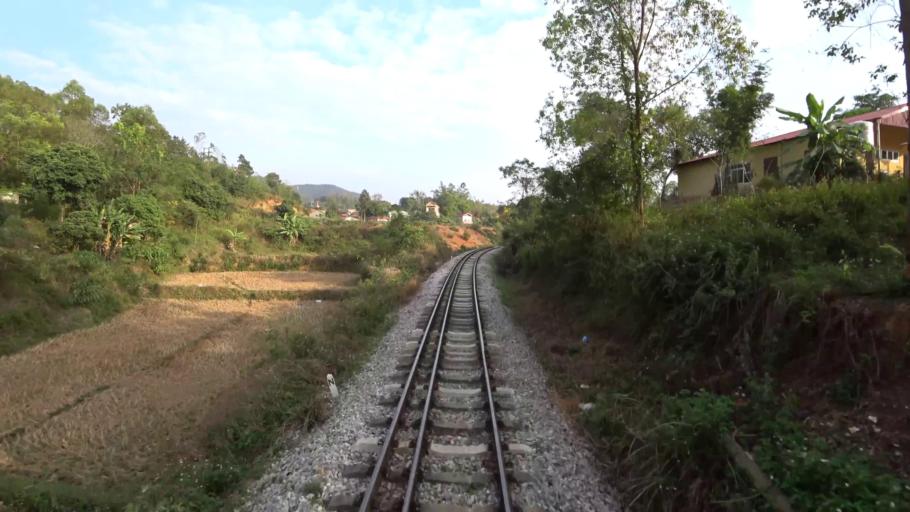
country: VN
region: Lang Son
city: Thi Tran Cao Loc
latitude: 21.9340
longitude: 106.6984
